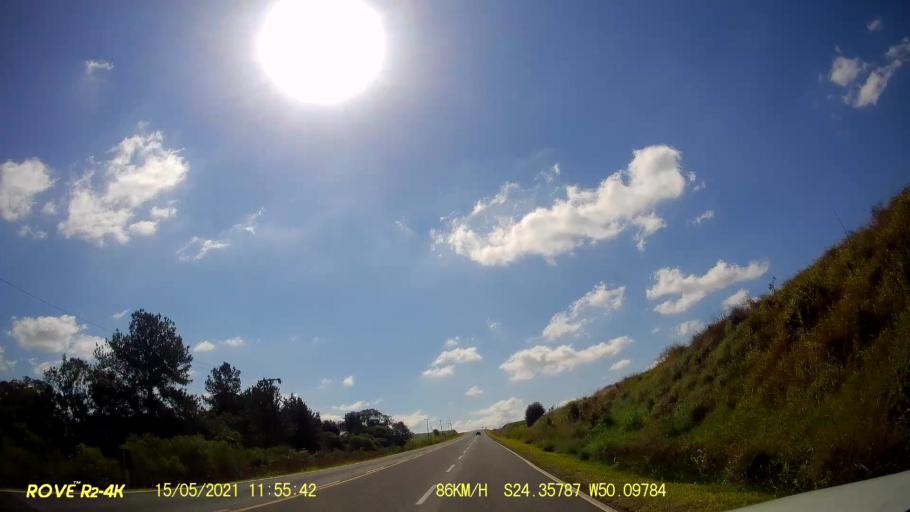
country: BR
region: Parana
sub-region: Pirai Do Sul
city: Pirai do Sul
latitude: -24.3579
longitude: -50.0978
